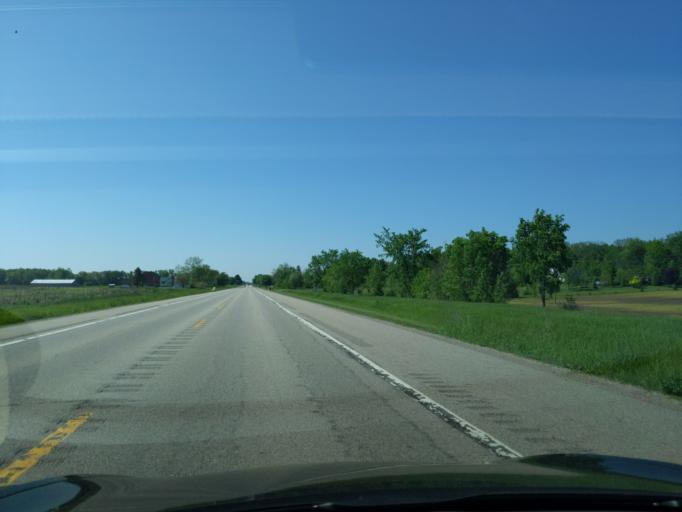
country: US
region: Michigan
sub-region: Ingham County
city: Stockbridge
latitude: 42.5367
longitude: -84.1911
